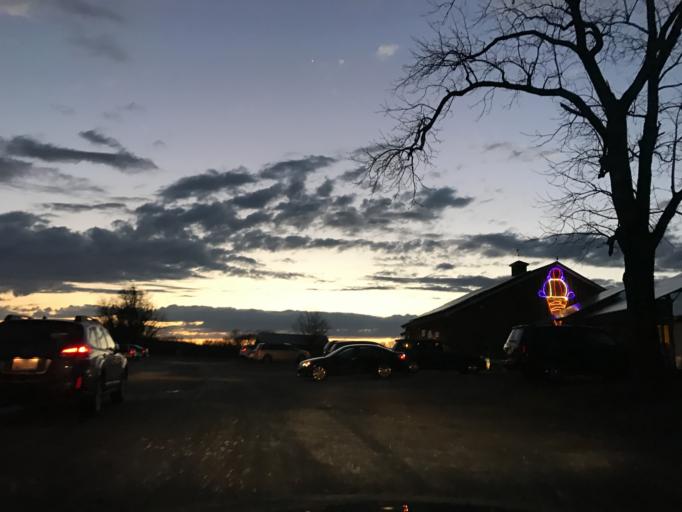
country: US
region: Maryland
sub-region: Harford County
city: Bel Air South
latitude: 39.5125
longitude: -76.2780
